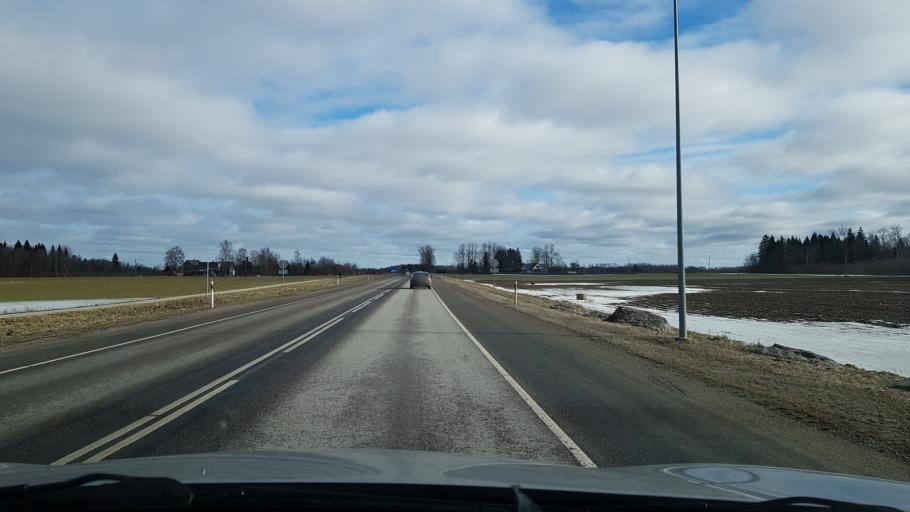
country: EE
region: Tartu
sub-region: UElenurme vald
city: Ulenurme
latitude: 58.3218
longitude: 26.6284
